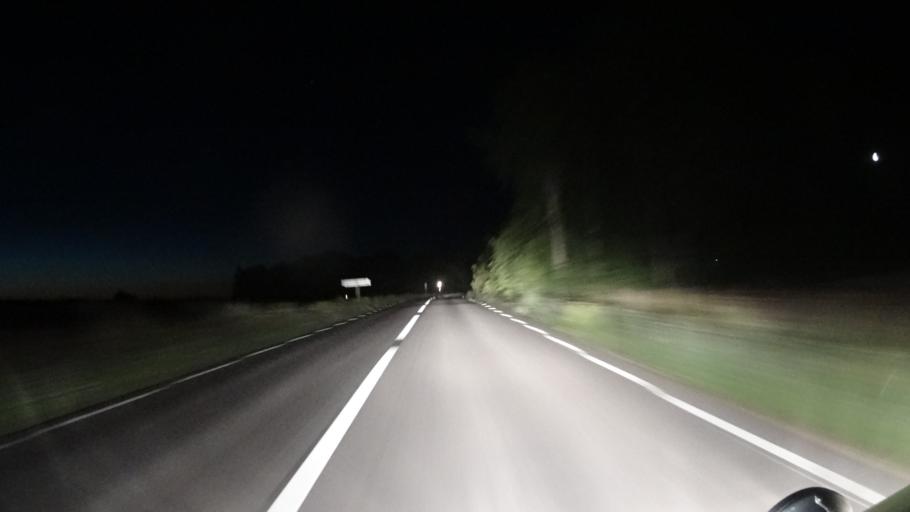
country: SE
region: OEstergoetland
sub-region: Odeshogs Kommun
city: OEdeshoeg
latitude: 58.2436
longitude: 14.7173
